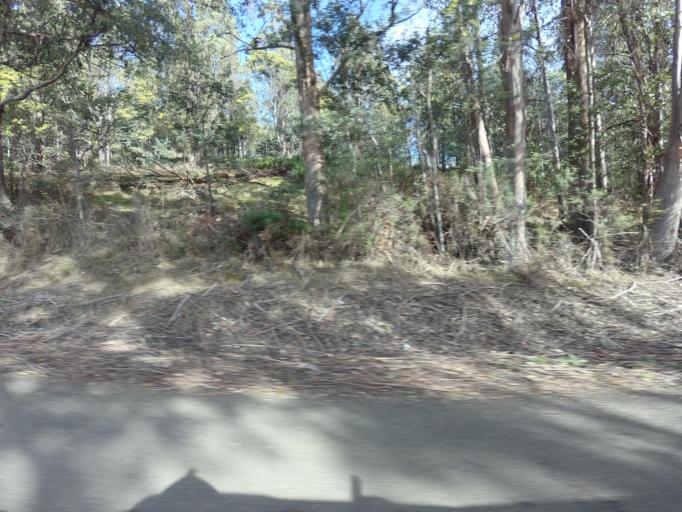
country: AU
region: Tasmania
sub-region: Kingborough
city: Margate
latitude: -43.0148
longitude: 147.1609
